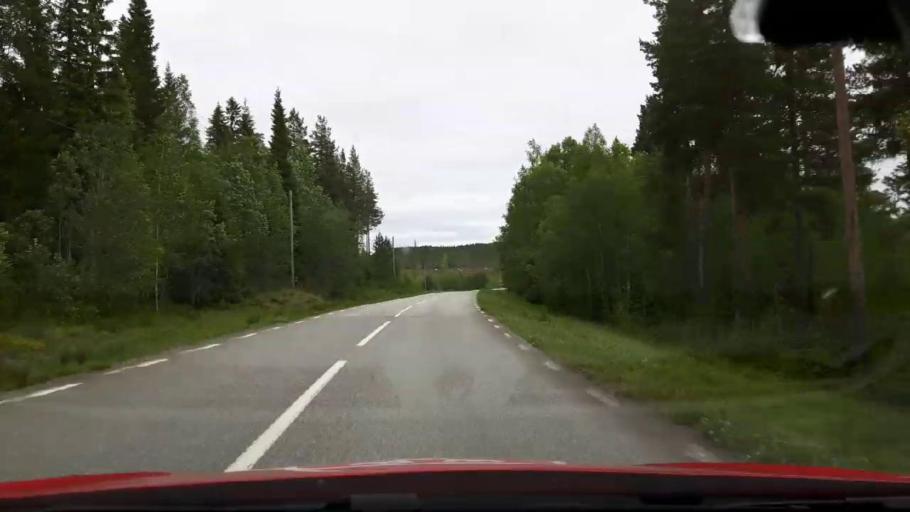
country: SE
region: Jaemtland
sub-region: Stroemsunds Kommun
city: Stroemsund
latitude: 63.3674
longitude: 15.7103
